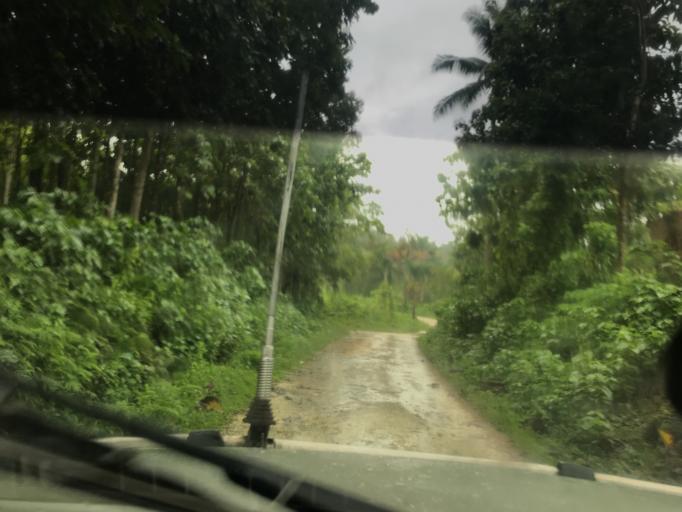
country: SB
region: Malaita
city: Auki
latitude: -9.0285
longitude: 160.7984
